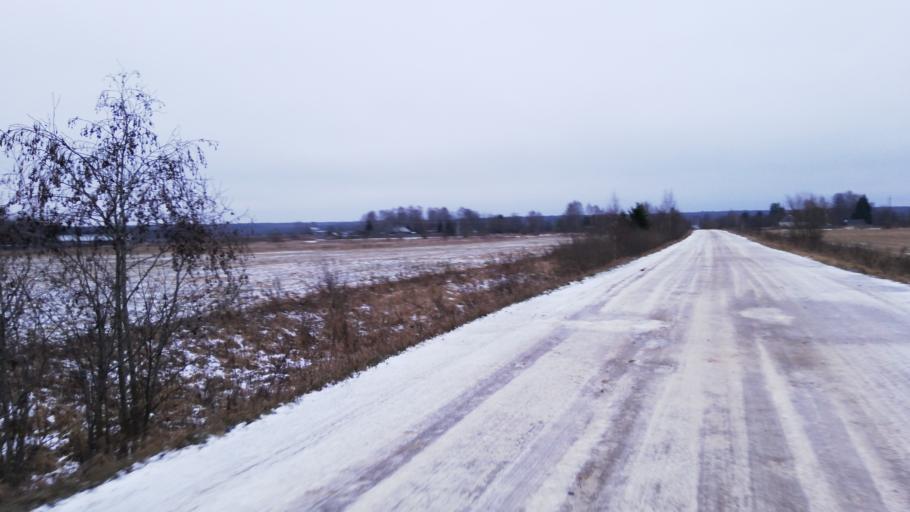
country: RU
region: Kostroma
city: Krasnoye-na-Volge
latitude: 57.6755
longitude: 41.1955
